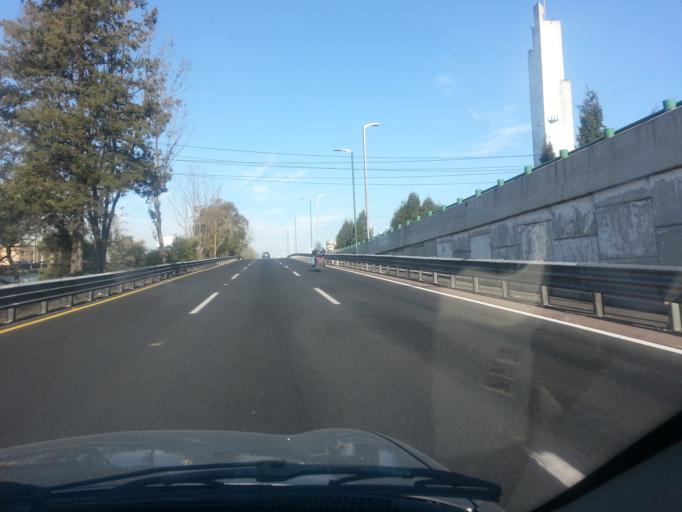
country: MX
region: Mexico
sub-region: San Mateo Atenco
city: Santa Maria la Asuncion
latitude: 19.2868
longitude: -99.5717
